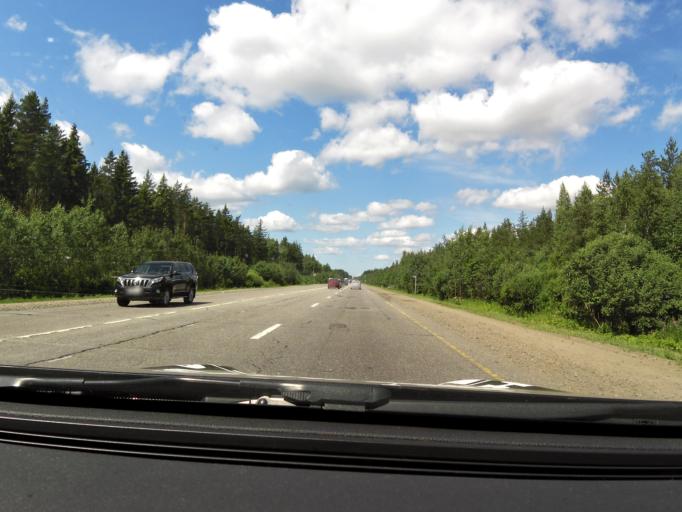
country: RU
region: Tverskaya
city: Kuzhenkino
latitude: 57.7352
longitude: 34.0383
